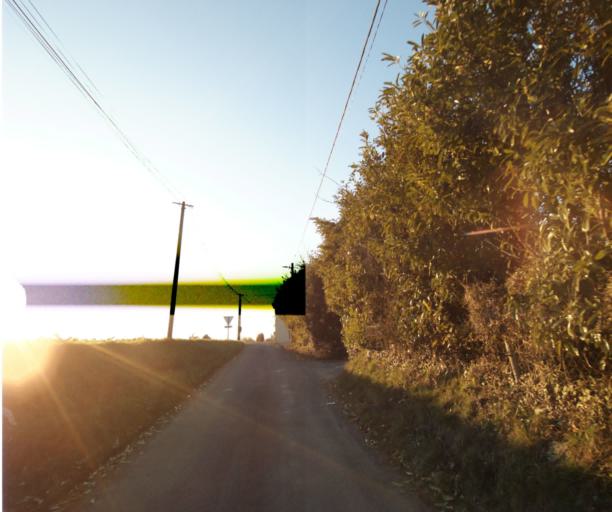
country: FR
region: Poitou-Charentes
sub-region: Departement des Deux-Sevres
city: Niort
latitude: 46.3536
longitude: -0.4401
